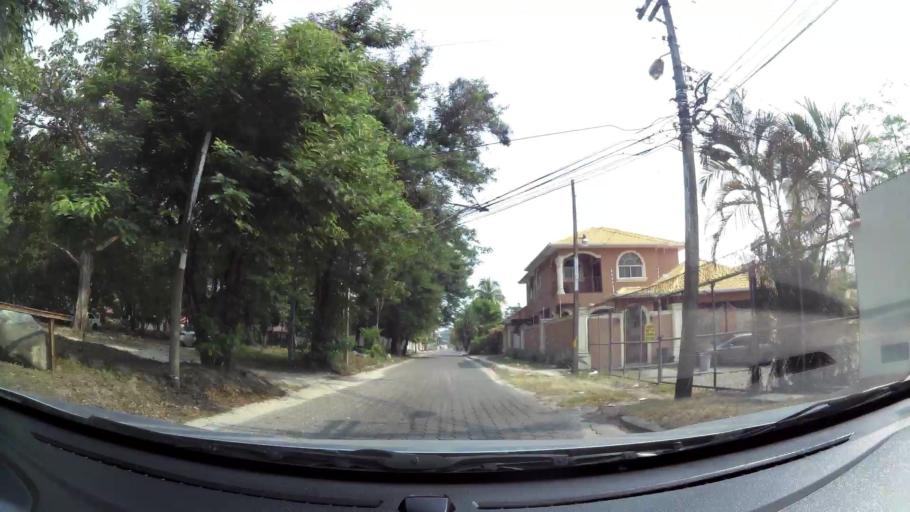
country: HN
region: Cortes
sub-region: San Pedro Sula
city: Pena Blanca
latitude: 15.5320
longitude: -88.0309
